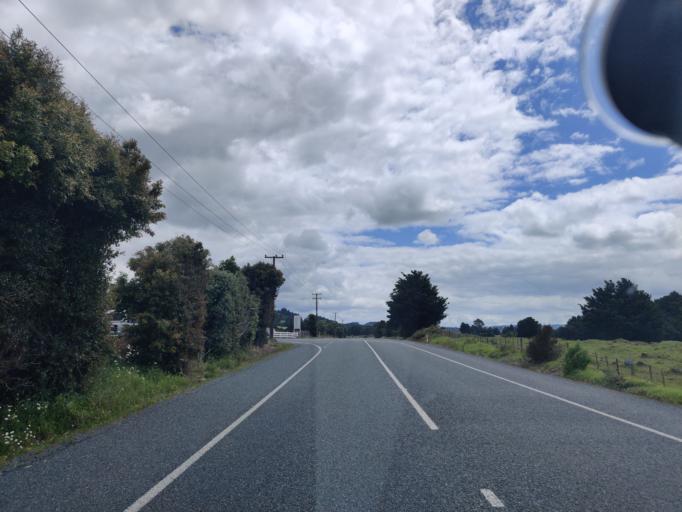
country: NZ
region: Northland
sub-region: Far North District
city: Kerikeri
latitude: -35.2934
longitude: 173.9845
